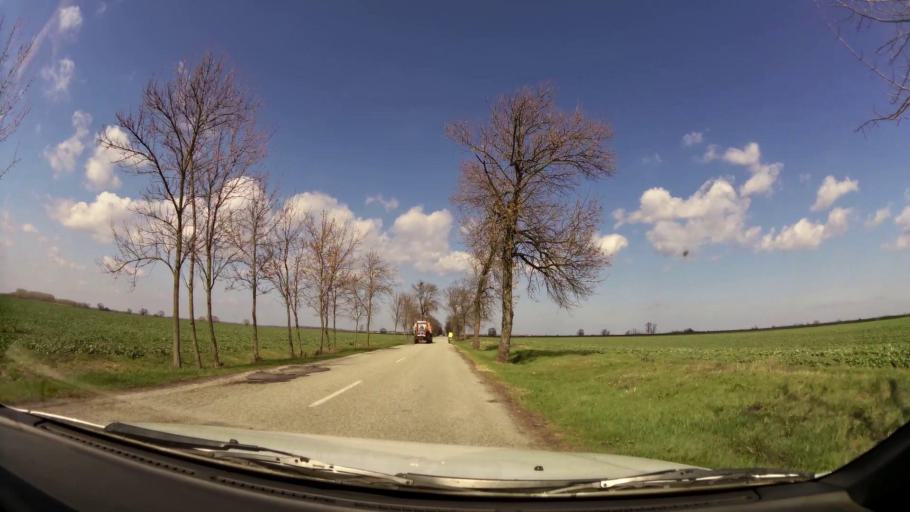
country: HU
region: Pest
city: Ujszilvas
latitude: 47.2986
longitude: 19.9381
